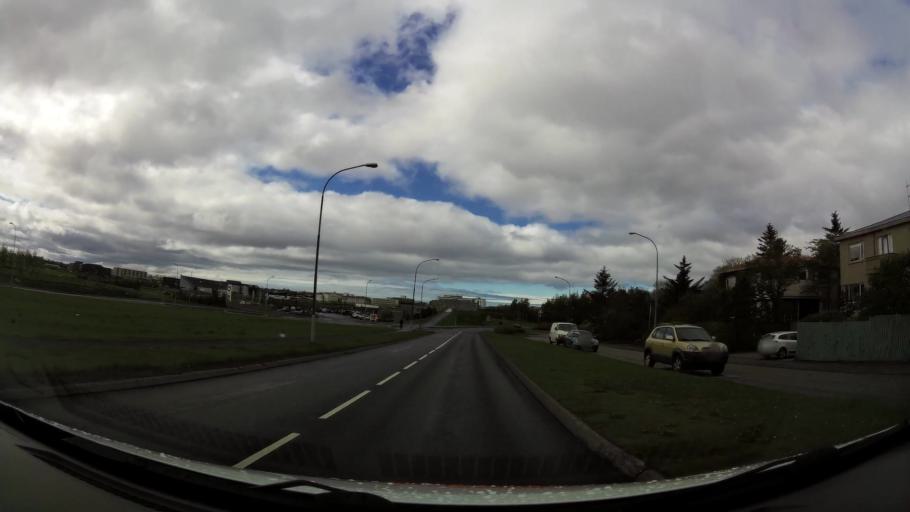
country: IS
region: Capital Region
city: Kopavogur
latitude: 64.1386
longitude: -21.9349
